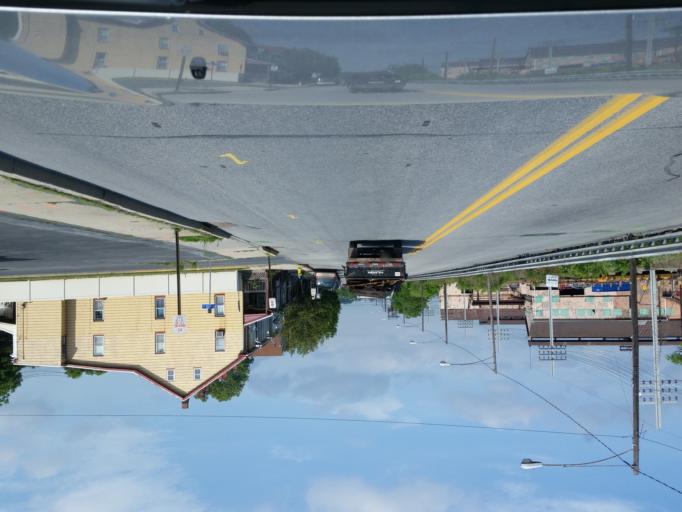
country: US
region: Pennsylvania
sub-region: Dauphin County
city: Enhaut
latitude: 40.2249
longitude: -76.8275
